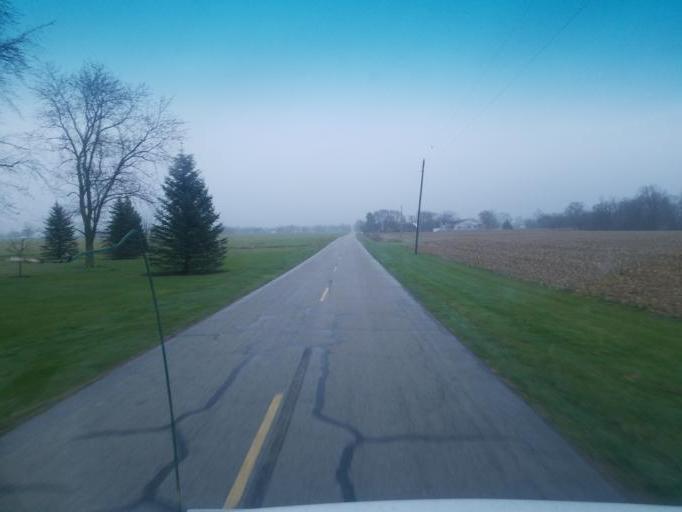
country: US
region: Ohio
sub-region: Henry County
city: Napoleon
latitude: 41.4135
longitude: -84.2037
